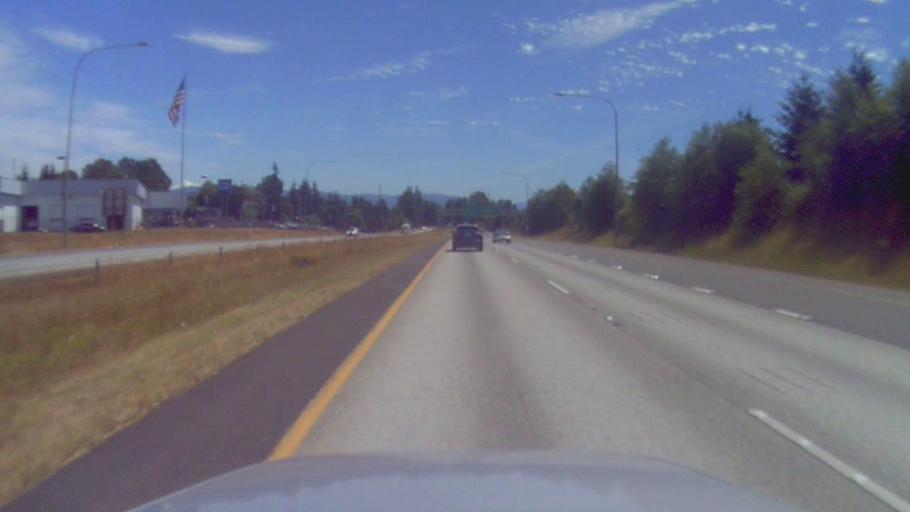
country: US
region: Washington
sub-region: Whatcom County
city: Bellingham
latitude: 48.7854
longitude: -122.5074
